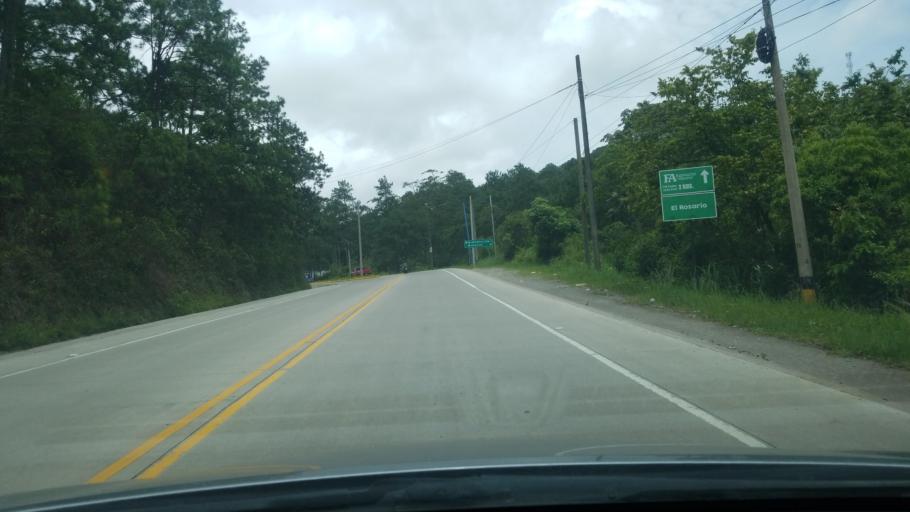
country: HN
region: Copan
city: Santa Rosa de Copan
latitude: 14.7991
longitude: -88.7771
